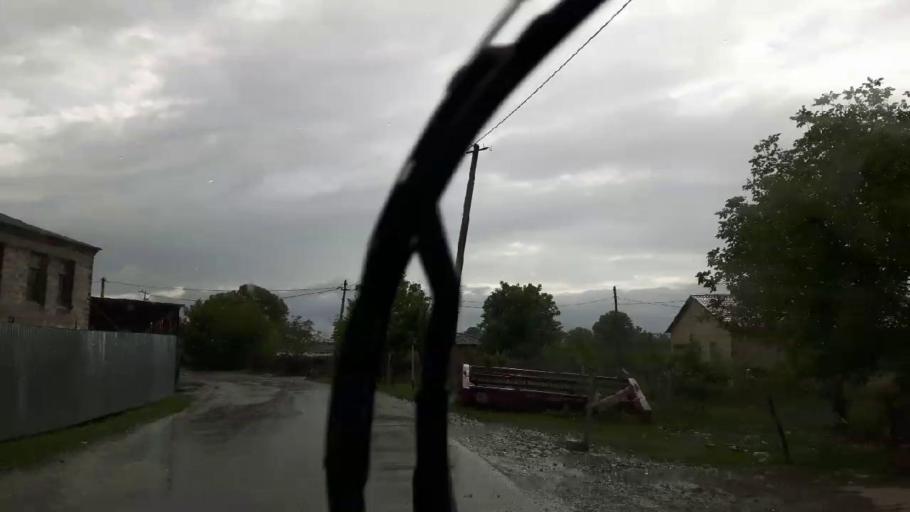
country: GE
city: Agara
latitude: 42.0094
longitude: 43.7646
